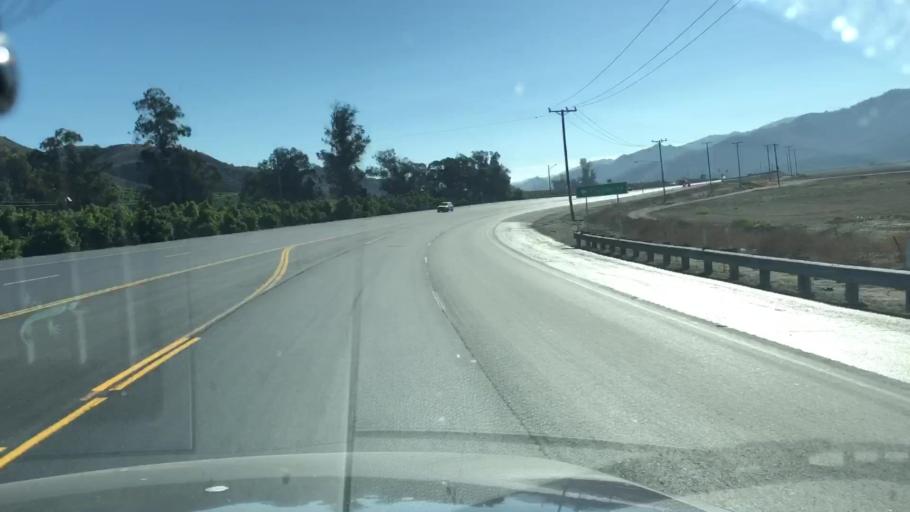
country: US
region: California
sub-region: Ventura County
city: Piru
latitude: 34.4110
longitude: -118.7822
